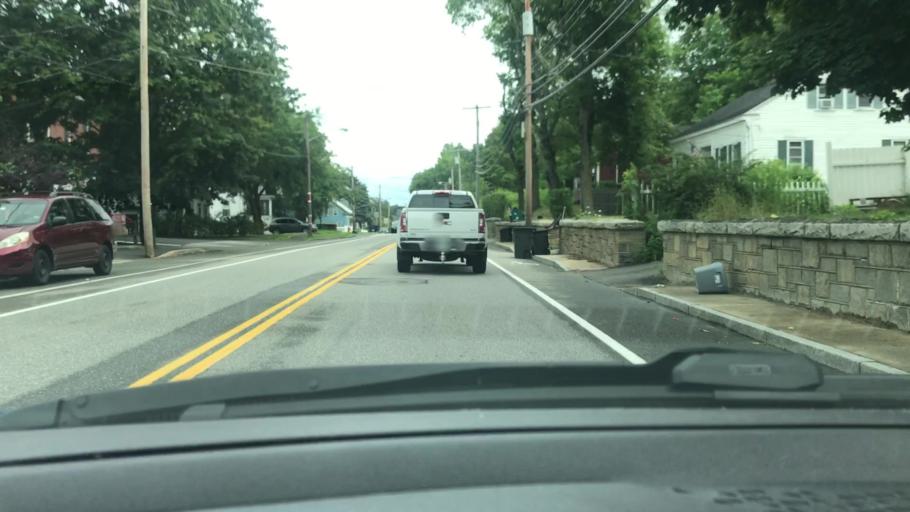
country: US
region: New Hampshire
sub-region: Merrimack County
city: East Concord
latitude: 43.2423
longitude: -71.5696
